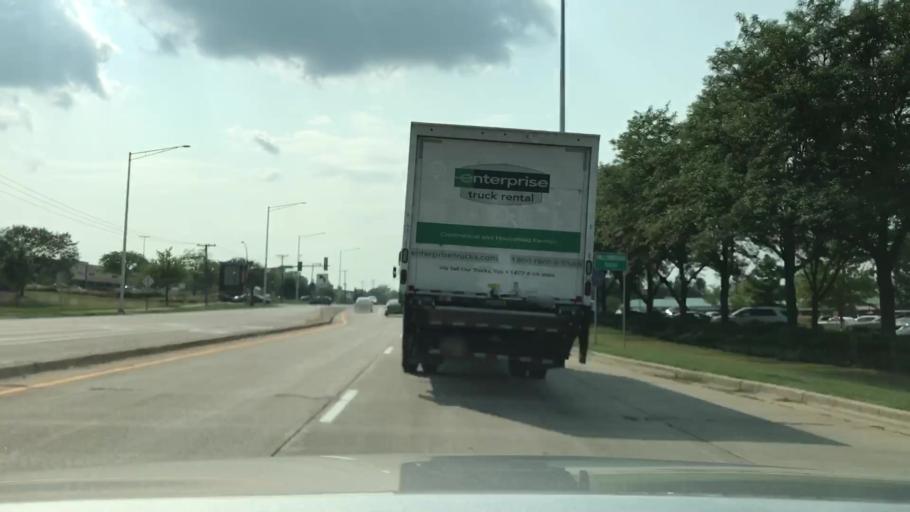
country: US
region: Illinois
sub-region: DuPage County
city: Willowbrook
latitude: 41.7744
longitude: -87.9472
